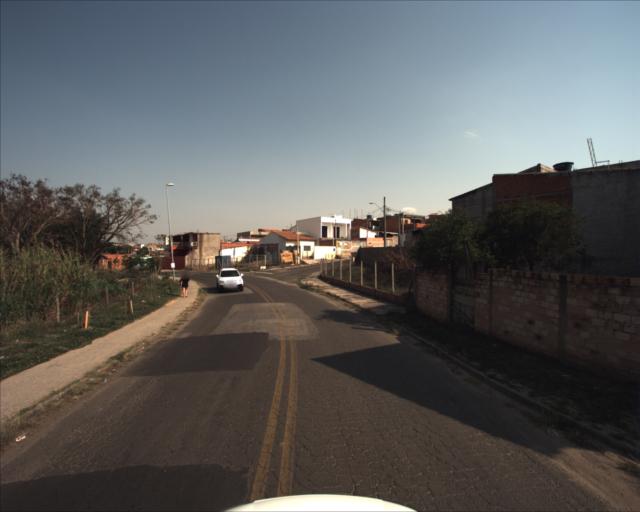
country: BR
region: Sao Paulo
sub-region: Sorocaba
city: Sorocaba
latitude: -23.4257
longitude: -47.4653
